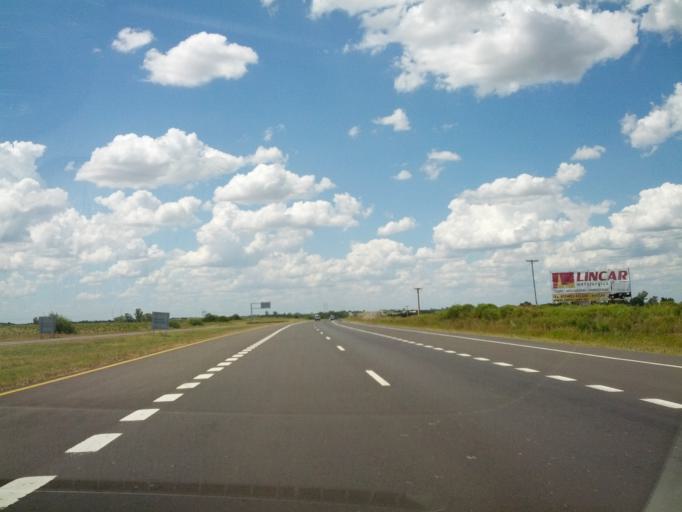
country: AR
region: Entre Rios
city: Colonia Elia
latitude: -32.5782
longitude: -58.3874
